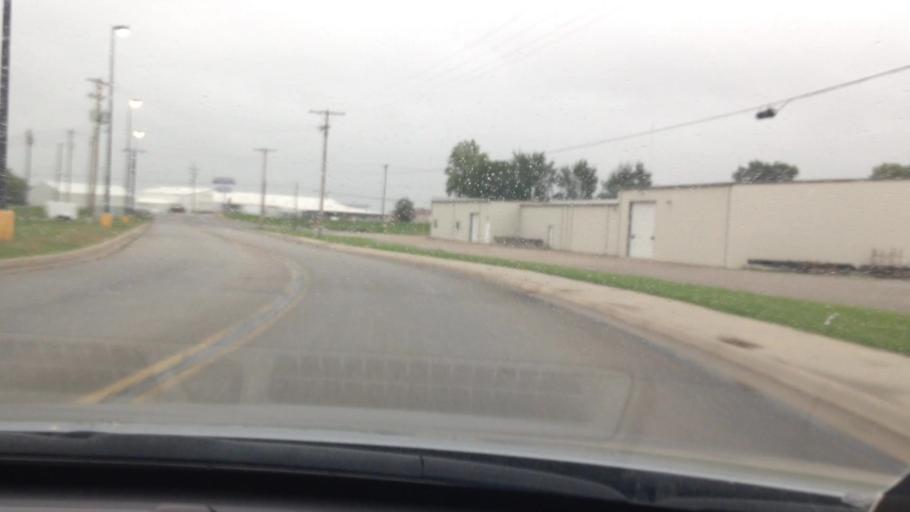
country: US
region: Kansas
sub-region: Brown County
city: Hiawatha
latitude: 39.8474
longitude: -95.5617
